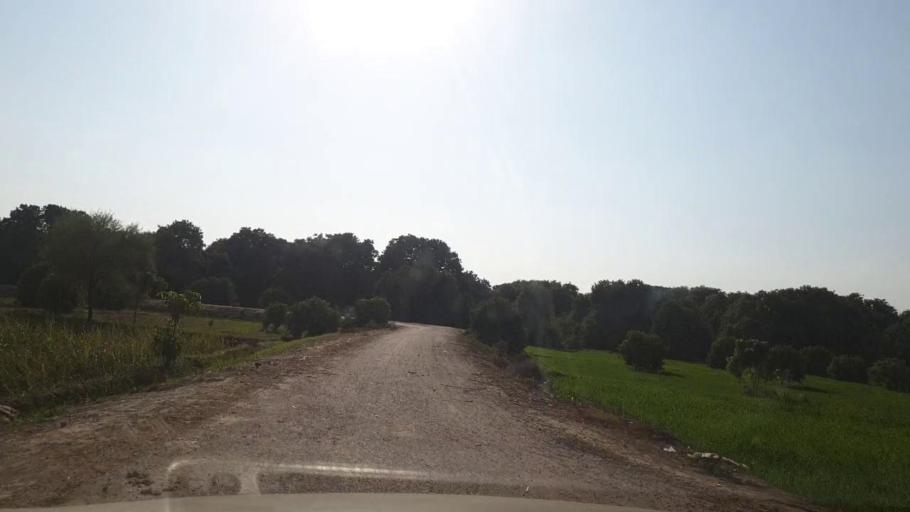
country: PK
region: Sindh
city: Tando Allahyar
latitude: 25.4925
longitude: 68.6456
